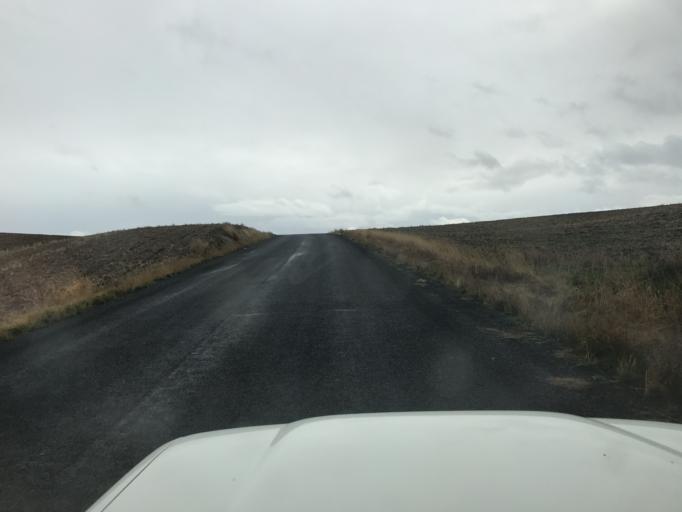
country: US
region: Idaho
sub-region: Latah County
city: Moscow
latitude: 46.7857
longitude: -116.9628
